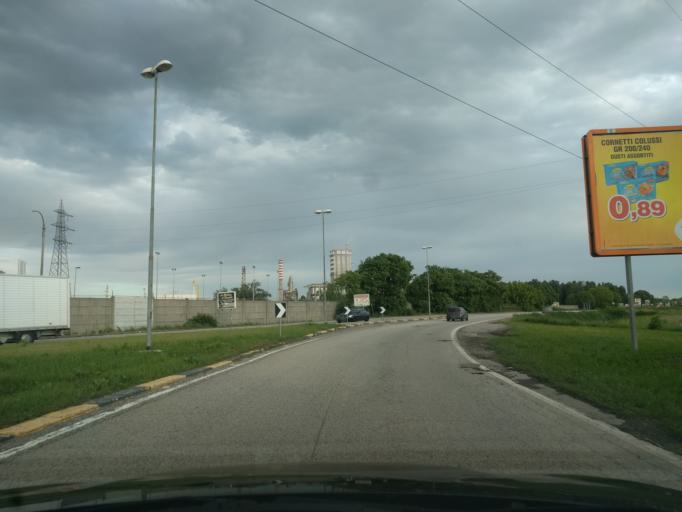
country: IT
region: Emilia-Romagna
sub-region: Provincia di Ferrara
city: Ferrara
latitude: 44.8577
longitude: 11.5822
